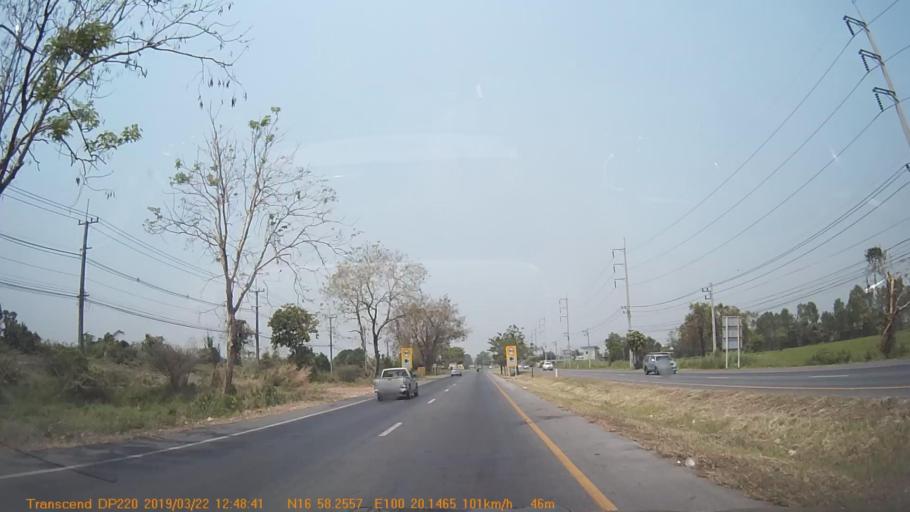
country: TH
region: Phitsanulok
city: Wat Bot
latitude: 16.9714
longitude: 100.3356
